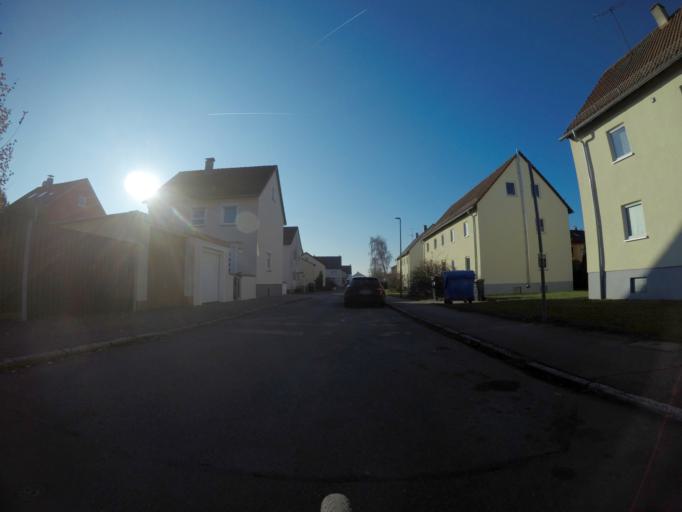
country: DE
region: Baden-Wuerttemberg
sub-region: Tuebingen Region
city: Reutlingen
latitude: 48.5079
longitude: 9.2151
